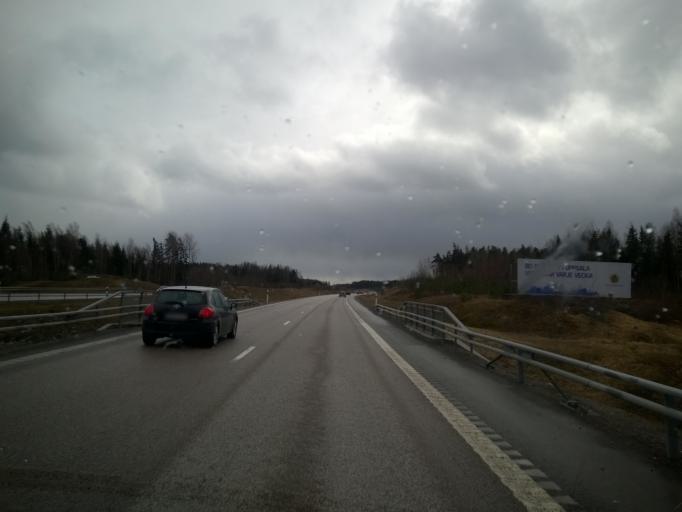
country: SE
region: Uppsala
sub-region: Osthammars Kommun
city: Bjorklinge
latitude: 60.0310
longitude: 17.6286
